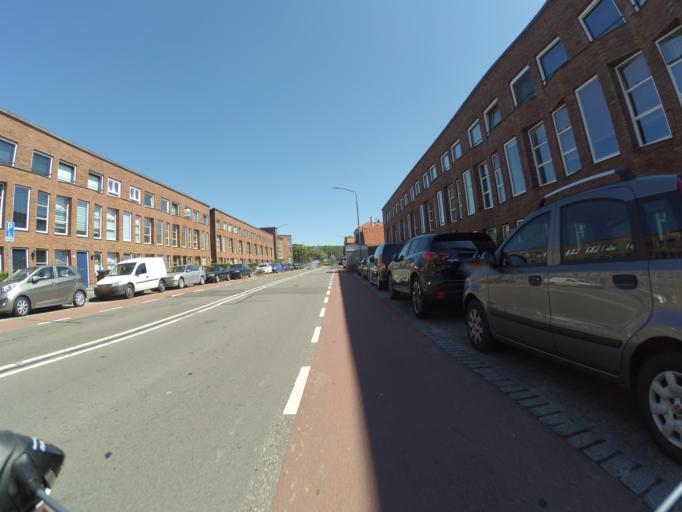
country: NL
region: South Holland
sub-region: Gemeente Dordrecht
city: Dordrecht
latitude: 51.8024
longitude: 4.6812
